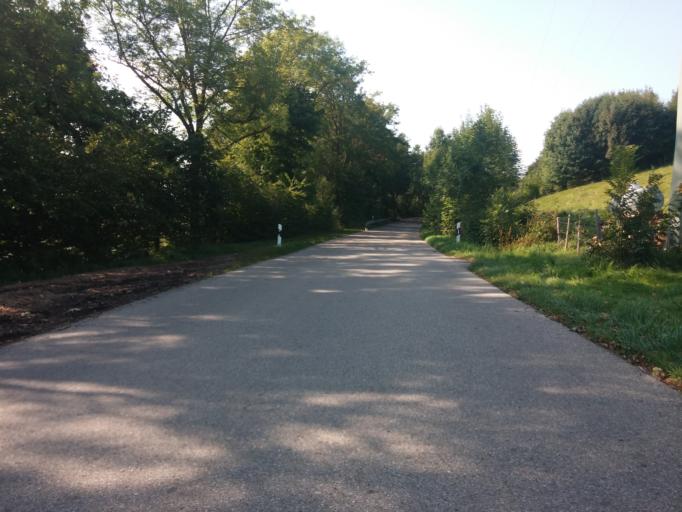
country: DE
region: Bavaria
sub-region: Swabia
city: Lautrach
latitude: 47.9182
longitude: 10.1243
